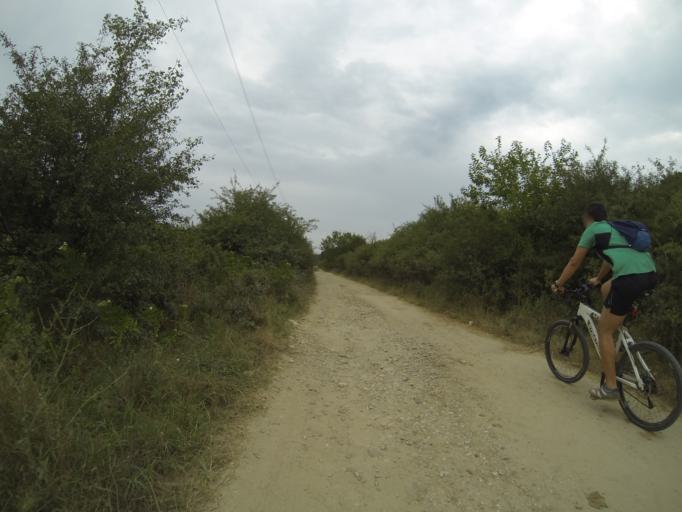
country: RO
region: Dolj
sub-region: Comuna Bradesti
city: Bradesti
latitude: 44.5079
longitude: 23.6424
